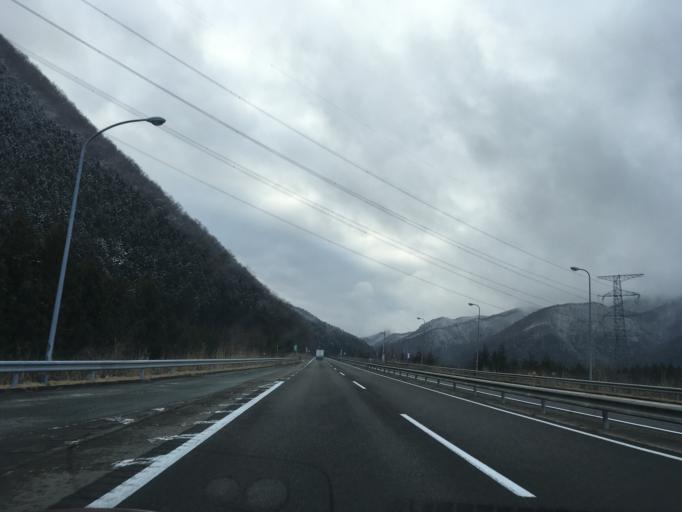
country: JP
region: Miyagi
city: Shiroishi
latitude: 38.1963
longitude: 140.5911
